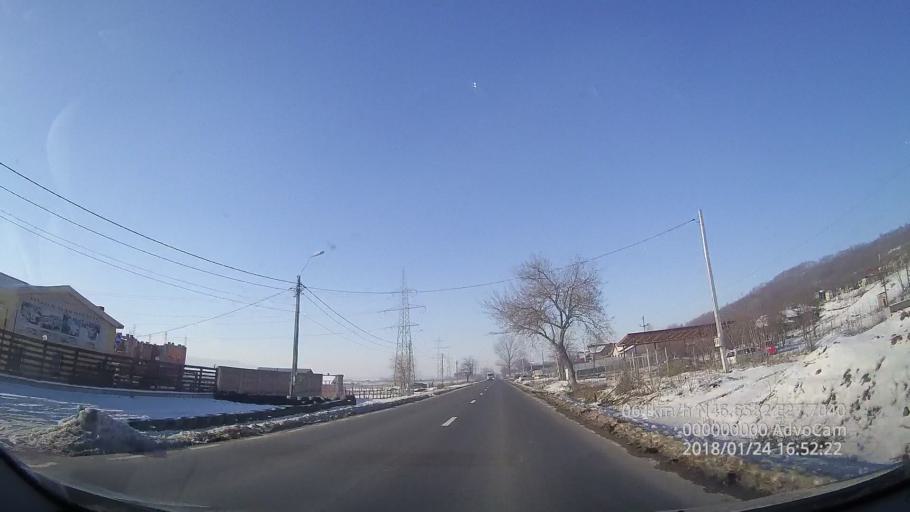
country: RO
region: Vaslui
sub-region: Municipiul Vaslui
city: Rediu
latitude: 46.6584
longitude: 27.7036
